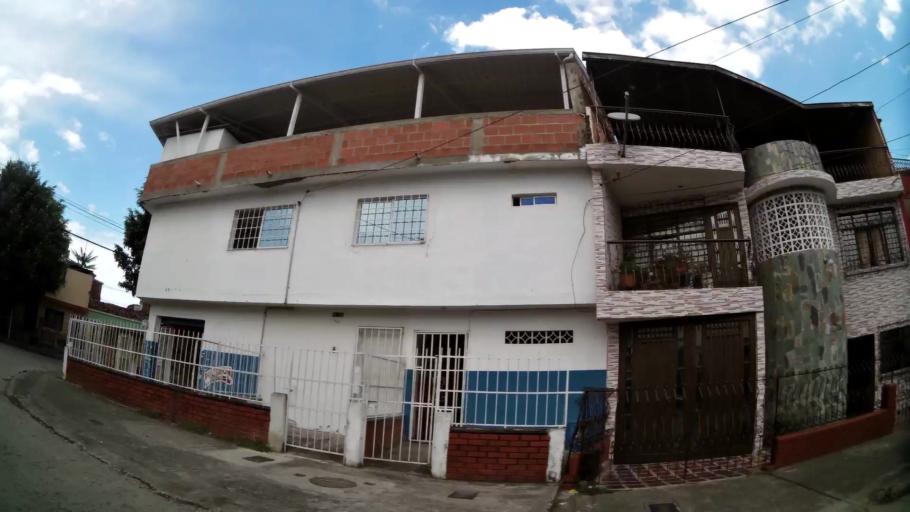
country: CO
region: Valle del Cauca
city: Cali
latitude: 3.4384
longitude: -76.5233
